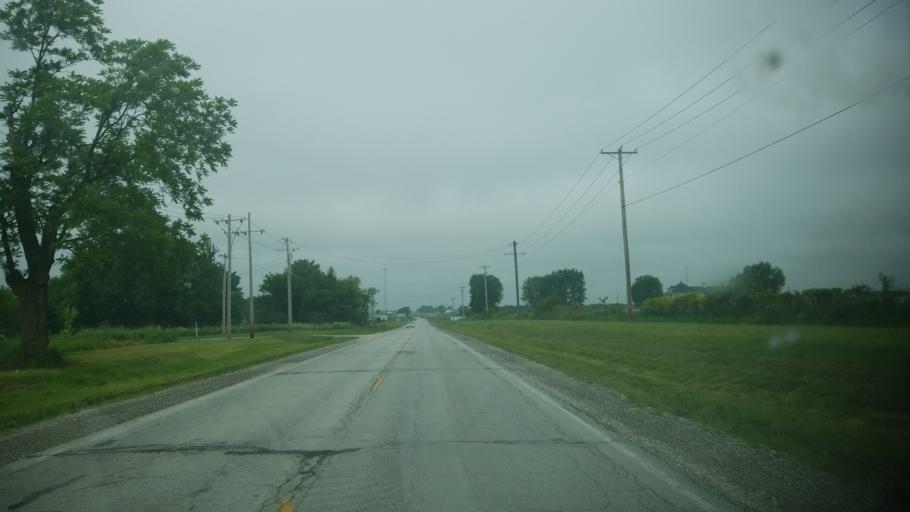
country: US
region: Missouri
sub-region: Pike County
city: Bowling Green
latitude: 39.3444
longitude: -91.2202
